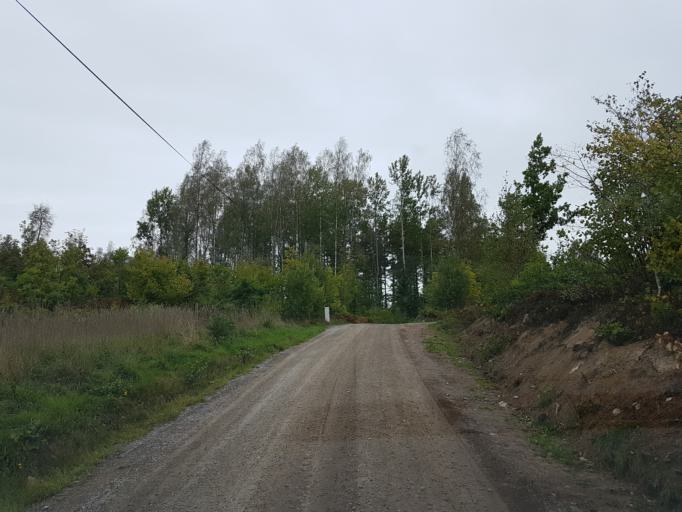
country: SE
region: OEstergoetland
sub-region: Atvidabergs Kommun
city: Atvidaberg
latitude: 58.2137
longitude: 16.0371
